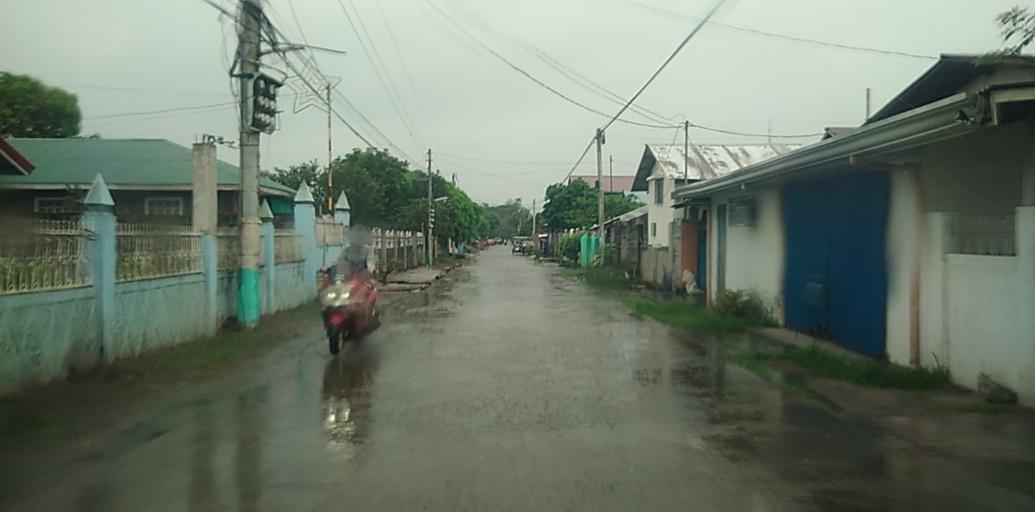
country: PH
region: Central Luzon
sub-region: Province of Pampanga
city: Arenas
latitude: 15.1753
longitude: 120.6819
